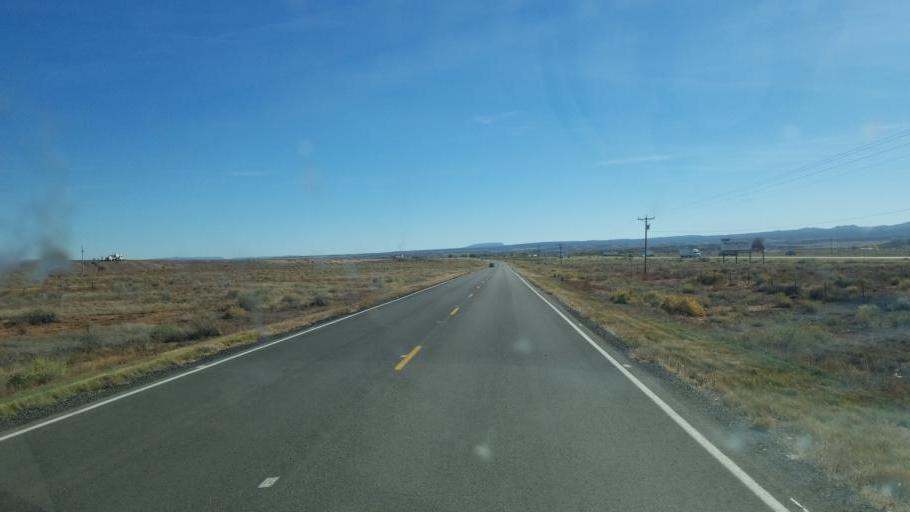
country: US
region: New Mexico
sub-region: Cibola County
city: Milan
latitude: 35.2933
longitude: -107.9866
